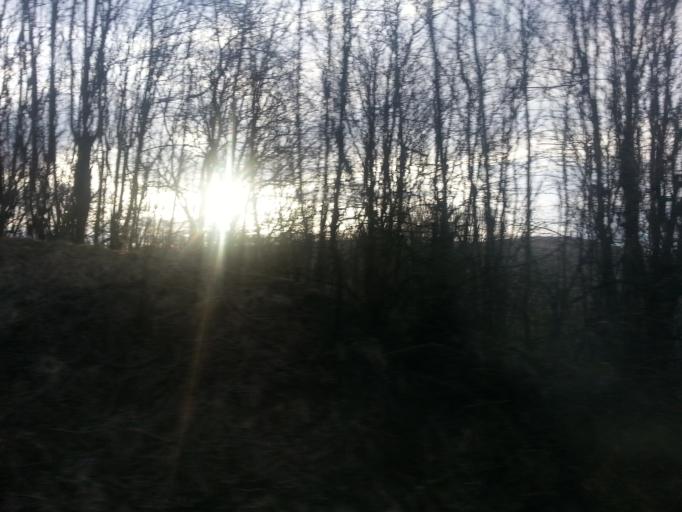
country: NO
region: Sor-Trondelag
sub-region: Trondheim
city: Trondheim
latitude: 63.3807
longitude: 10.3583
